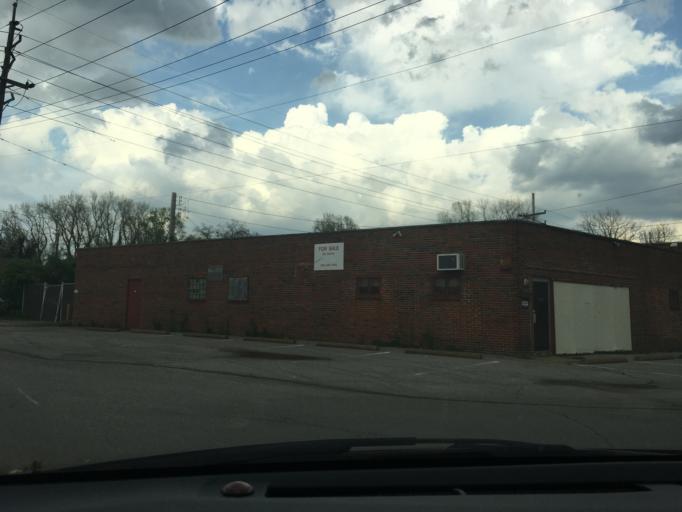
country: US
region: Missouri
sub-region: Saint Louis County
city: Berkeley
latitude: 38.7542
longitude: -90.3316
